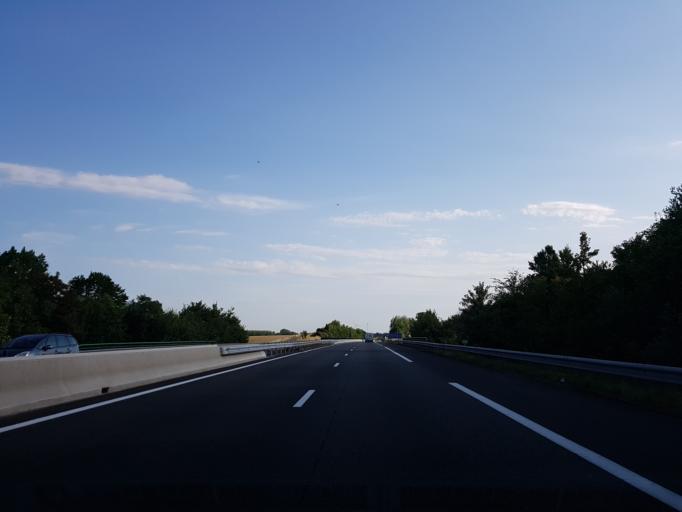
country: FR
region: Nord-Pas-de-Calais
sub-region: Departement du Nord
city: Raillencourt-Sainte-Olle
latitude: 50.1722
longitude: 3.1806
